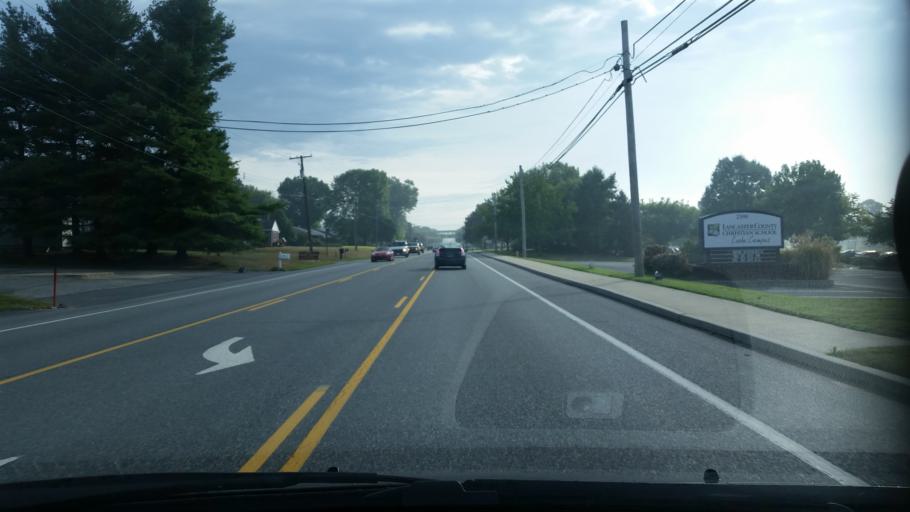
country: US
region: Pennsylvania
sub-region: Lancaster County
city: Brownstown
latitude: 40.0840
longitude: -76.2281
